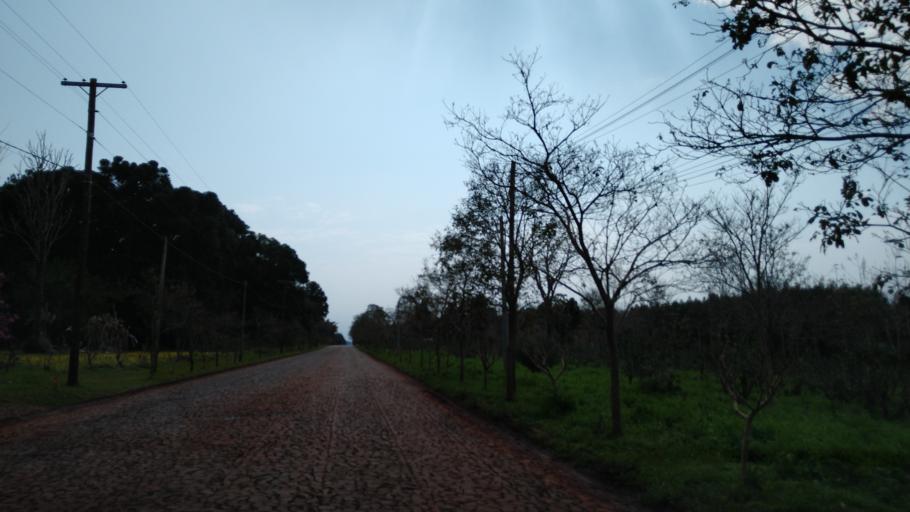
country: AR
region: Misiones
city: Ruiz de Montoya
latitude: -26.9568
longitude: -55.0559
